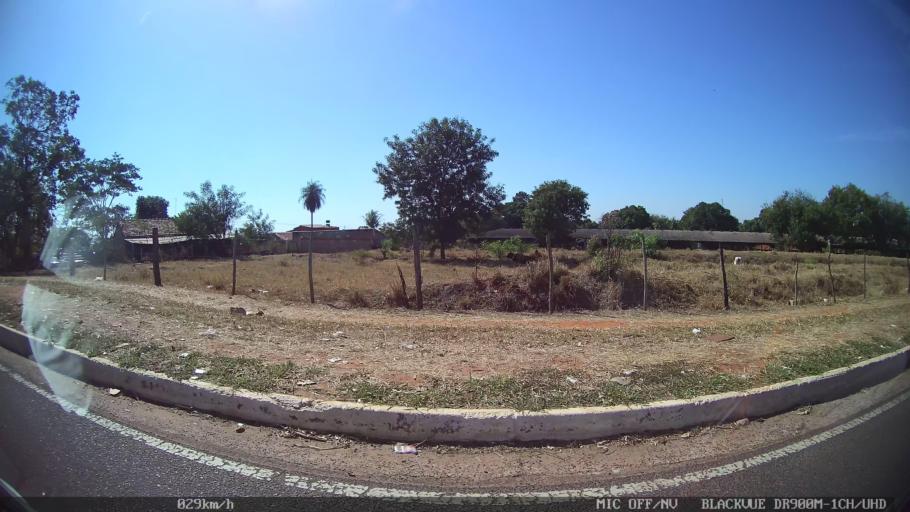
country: BR
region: Sao Paulo
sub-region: Sao Jose Do Rio Preto
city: Sao Jose do Rio Preto
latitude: -20.7680
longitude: -49.4196
